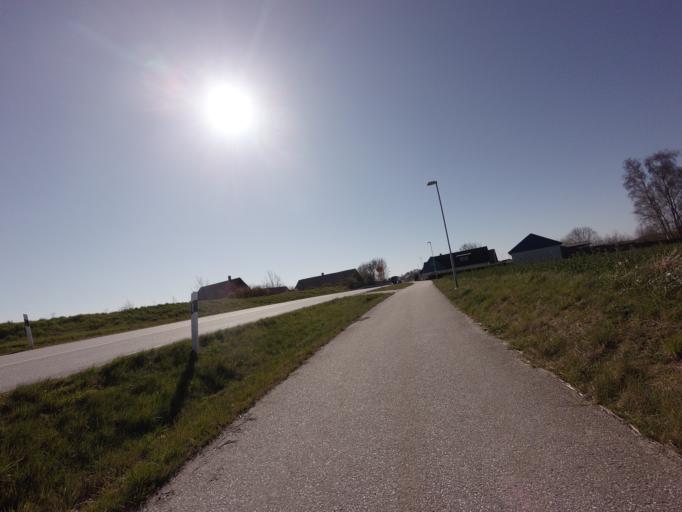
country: SE
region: Skane
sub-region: Malmo
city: Oxie
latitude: 55.4753
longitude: 13.1322
